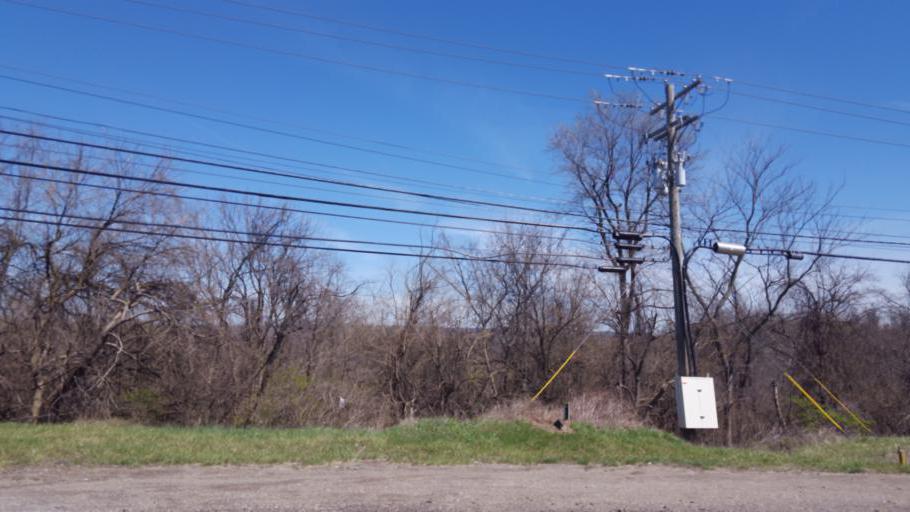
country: US
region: Ohio
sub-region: Belmont County
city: Saint Clairsville
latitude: 40.0724
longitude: -80.8595
